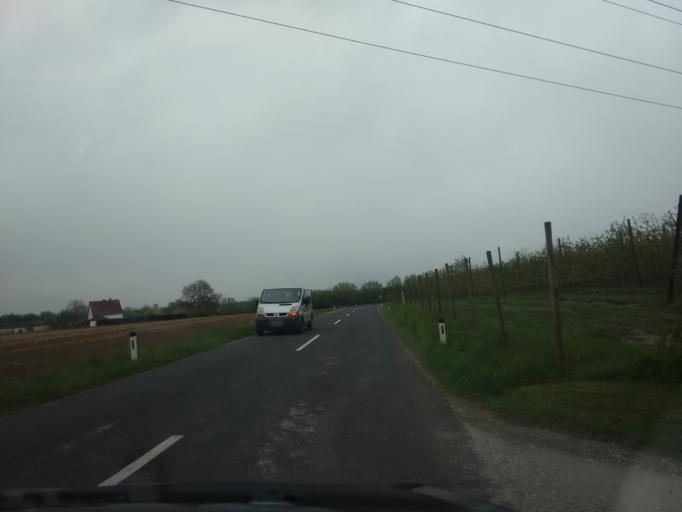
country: AT
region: Upper Austria
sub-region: Wels-Land
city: Holzhausen
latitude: 48.2141
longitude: 14.0895
